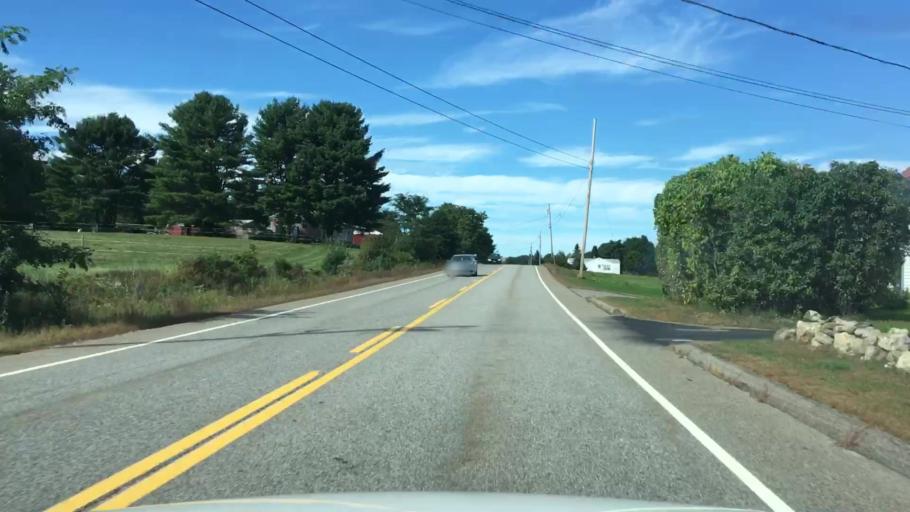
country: US
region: Maine
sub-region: Cumberland County
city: Westbrook
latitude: 43.6618
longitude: -70.4041
